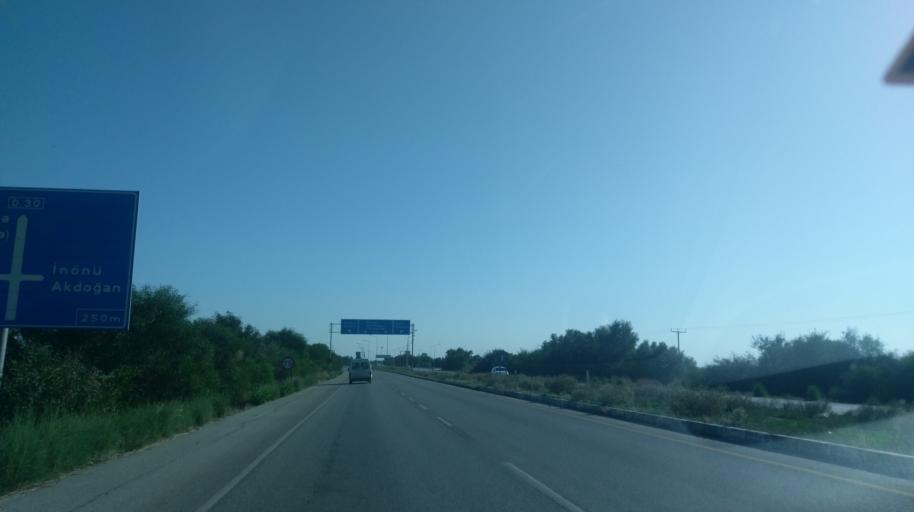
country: CY
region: Ammochostos
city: Lefkonoiko
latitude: 35.1832
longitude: 33.6971
